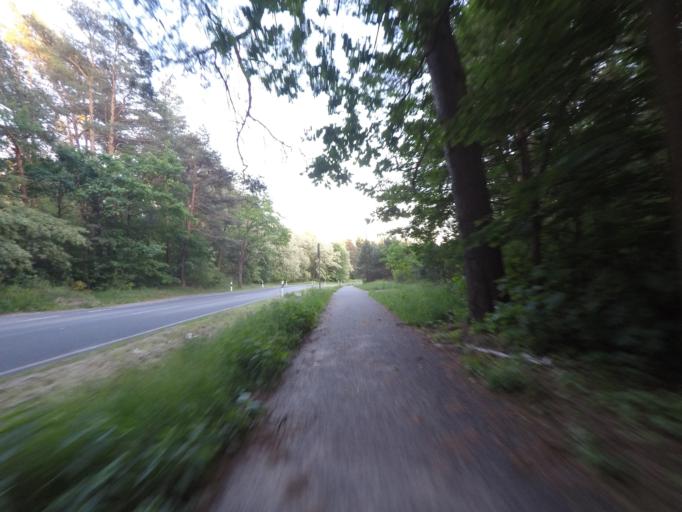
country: DE
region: Brandenburg
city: Marienwerder
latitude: 52.8595
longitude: 13.6494
